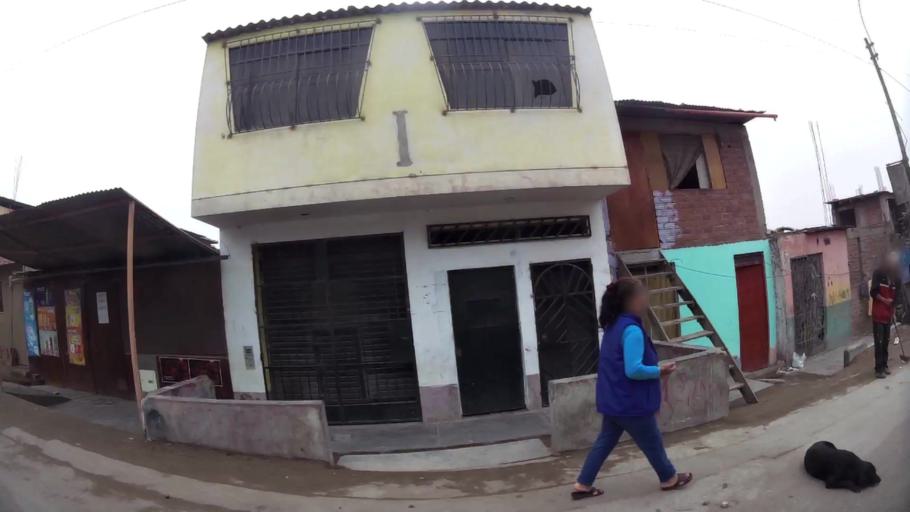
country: PE
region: Lima
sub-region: Lima
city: Surco
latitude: -12.1817
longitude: -76.9258
